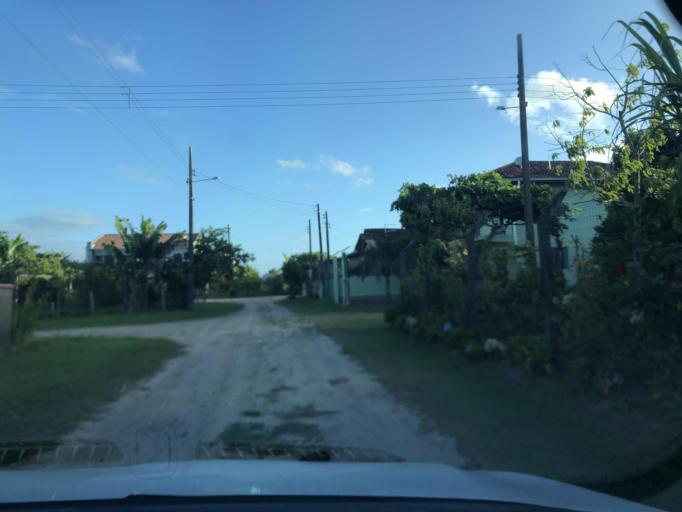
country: BR
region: Santa Catarina
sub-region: Sao Francisco Do Sul
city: Sao Francisco do Sul
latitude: -26.2259
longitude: -48.5263
